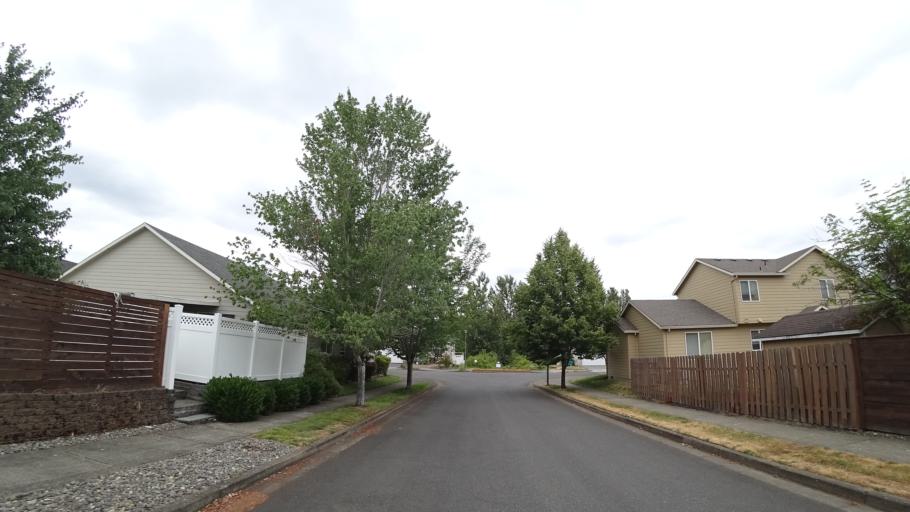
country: US
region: Washington
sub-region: Clark County
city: Vancouver
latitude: 45.5898
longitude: -122.6461
